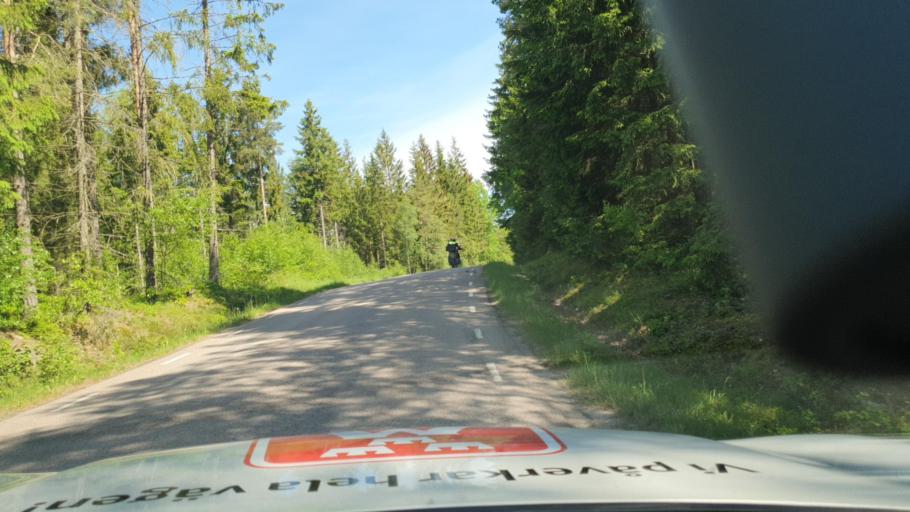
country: SE
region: Vaestra Goetaland
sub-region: Herrljunga Kommun
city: Herrljunga
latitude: 58.0124
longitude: 13.0911
